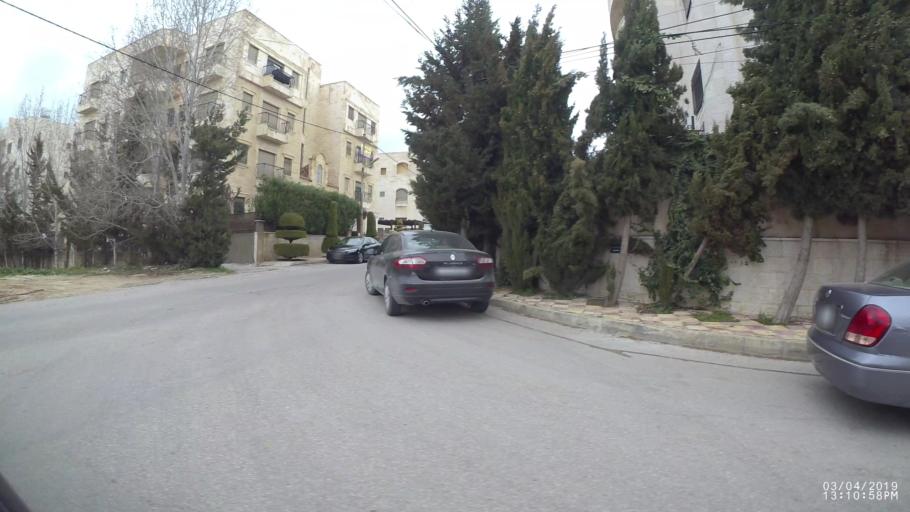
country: JO
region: Amman
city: Wadi as Sir
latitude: 31.9630
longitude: 35.8274
